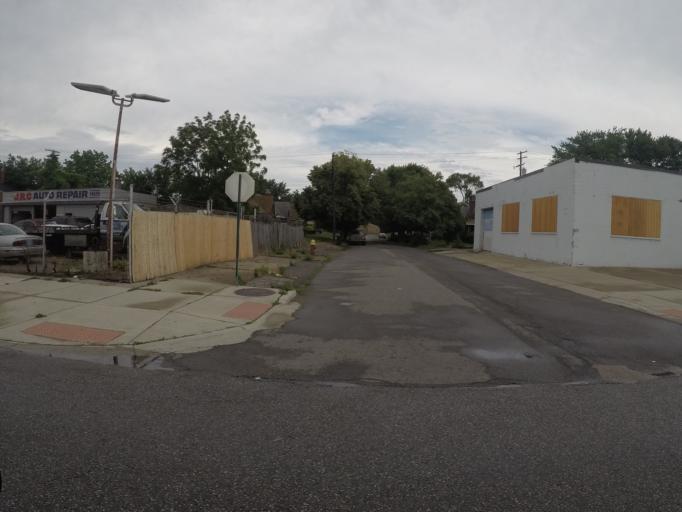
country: US
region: Michigan
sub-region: Wayne County
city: Grosse Pointe Park
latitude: 42.3963
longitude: -82.9570
